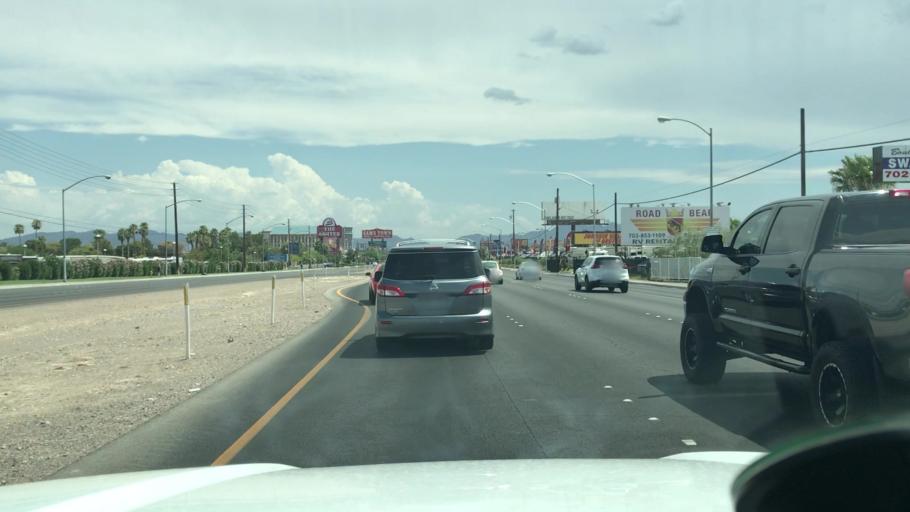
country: US
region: Nevada
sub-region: Clark County
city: Winchester
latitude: 36.1190
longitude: -115.0715
